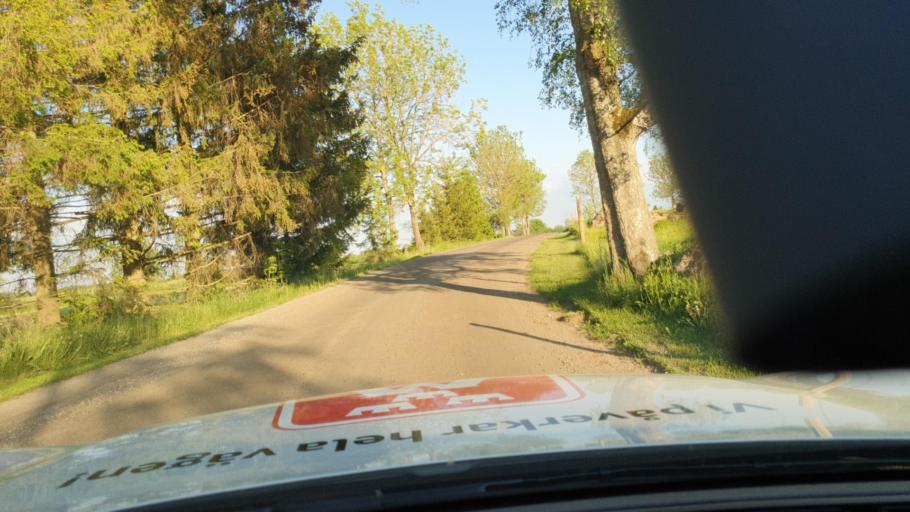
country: SE
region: Vaestra Goetaland
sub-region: Falkopings Kommun
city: Falkoeping
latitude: 58.0646
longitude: 13.6234
